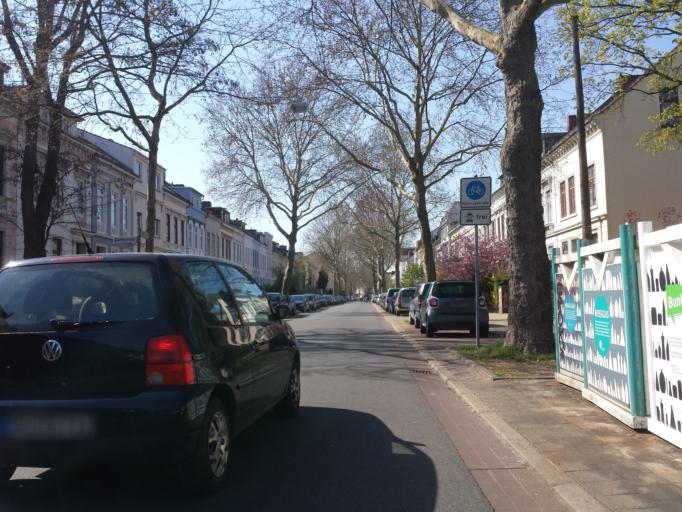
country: DE
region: Bremen
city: Bremen
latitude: 53.0745
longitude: 8.8302
